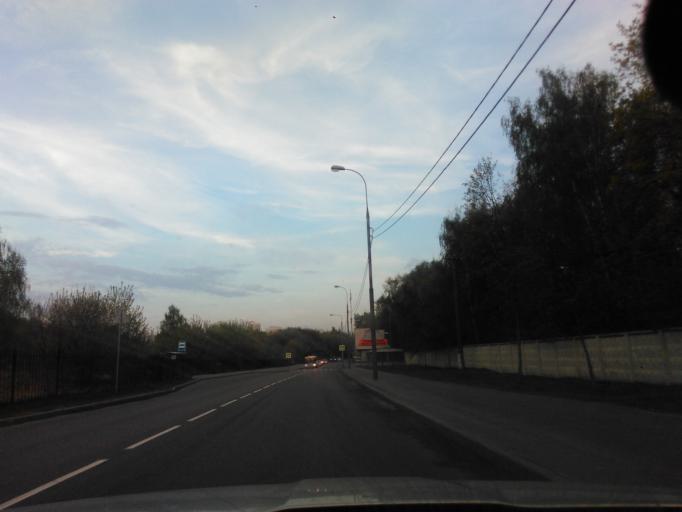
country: RU
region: Moscow
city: Kuz'minki
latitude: 55.6826
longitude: 37.7853
